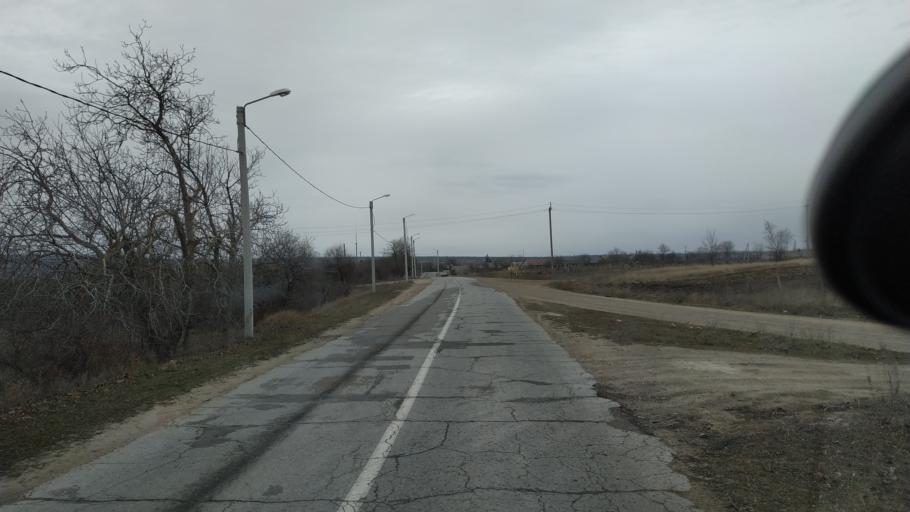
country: MD
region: Telenesti
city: Cocieri
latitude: 47.3359
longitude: 29.0980
